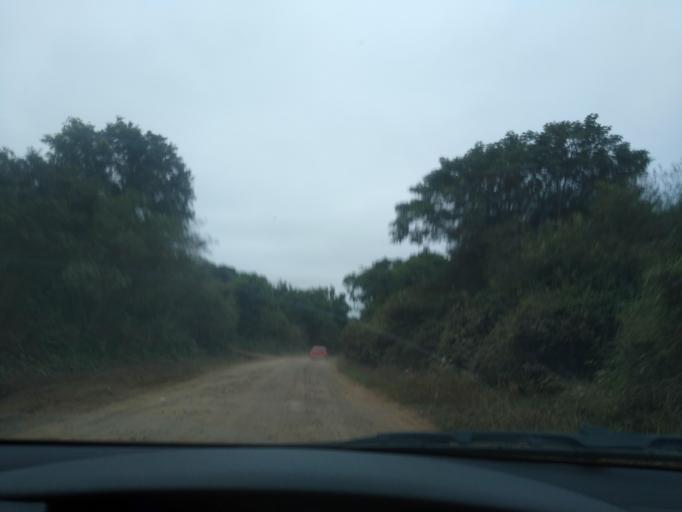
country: AR
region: Chaco
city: Colonia Benitez
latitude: -27.3391
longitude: -58.9689
